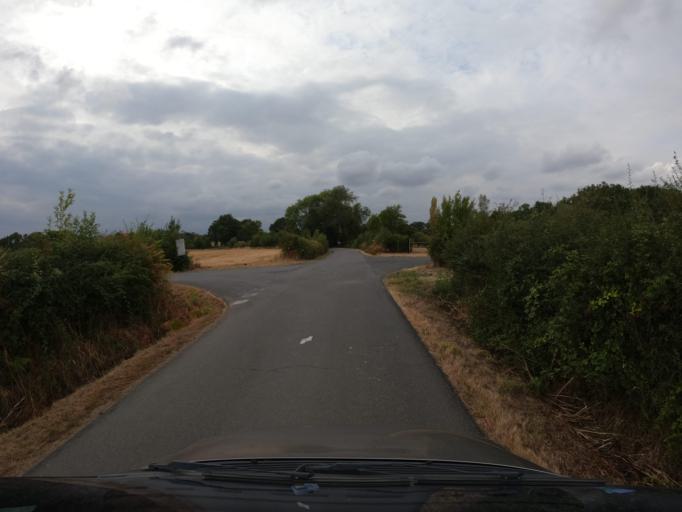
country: FR
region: Pays de la Loire
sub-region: Departement de Maine-et-Loire
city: La Romagne
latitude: 47.0450
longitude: -0.9842
